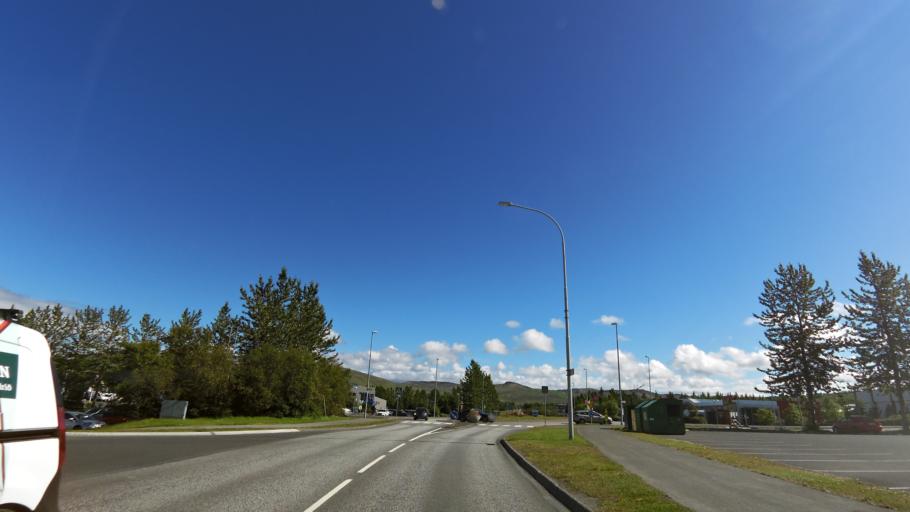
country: IS
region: Capital Region
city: Mosfellsbaer
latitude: 64.1669
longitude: -21.6966
